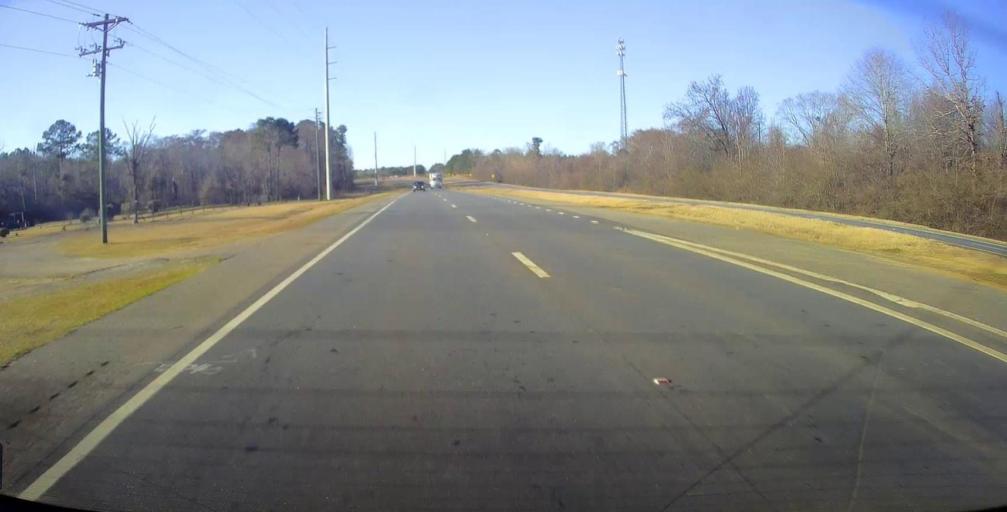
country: US
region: Georgia
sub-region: Lee County
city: Leesburg
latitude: 31.8854
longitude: -84.2451
